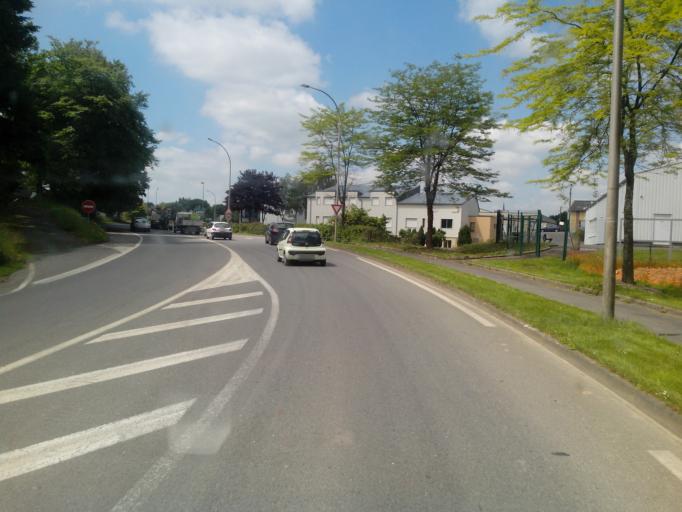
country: FR
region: Brittany
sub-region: Departement d'Ille-et-Vilaine
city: Lecousse
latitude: 48.3683
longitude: -1.2065
